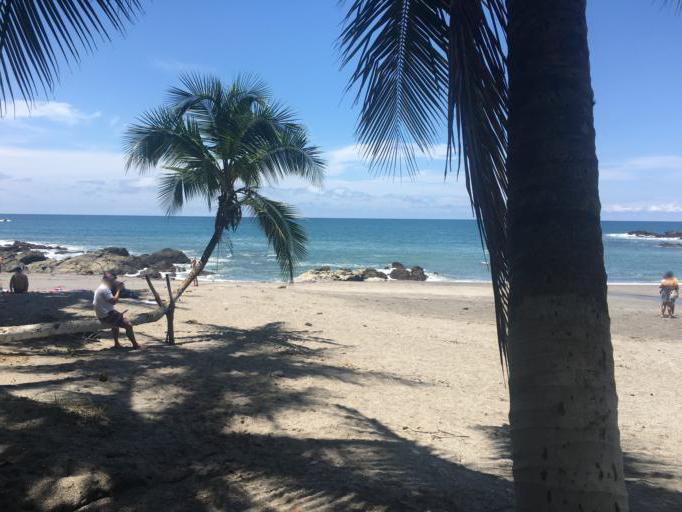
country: CR
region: Puntarenas
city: Paquera
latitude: 9.6545
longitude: -85.0680
